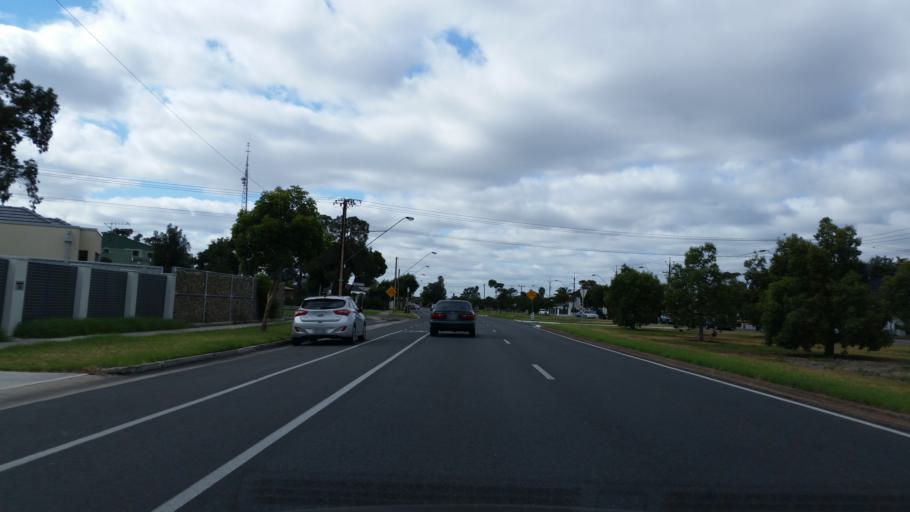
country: AU
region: South Australia
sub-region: City of West Torrens
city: Plympton
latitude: -34.9312
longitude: 138.5418
